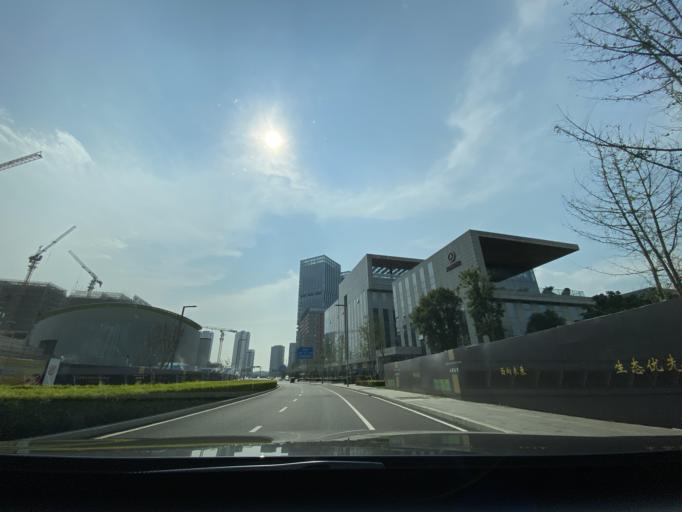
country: CN
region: Sichuan
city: Dongsheng
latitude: 30.3957
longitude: 104.0750
